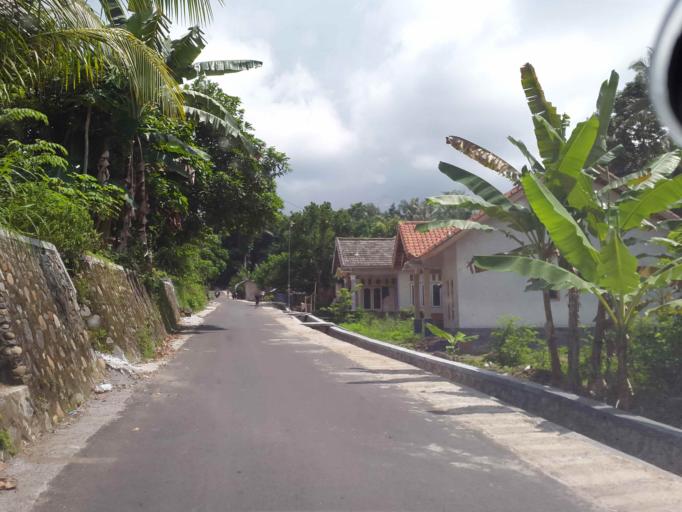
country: ID
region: West Nusa Tenggara
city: Penimbung Barat
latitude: -8.5332
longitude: 116.1537
